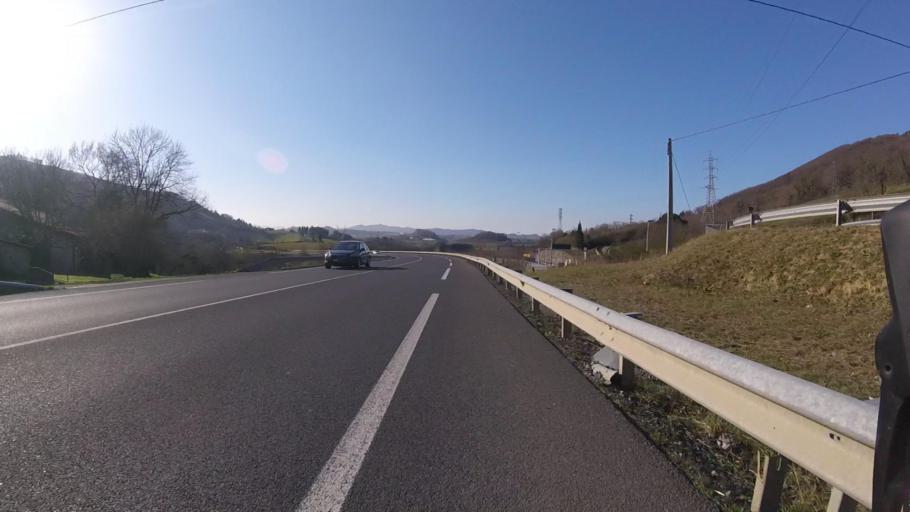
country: ES
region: Basque Country
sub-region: Provincia de Guipuzcoa
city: Astigarraga
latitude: 43.2828
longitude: -1.9193
